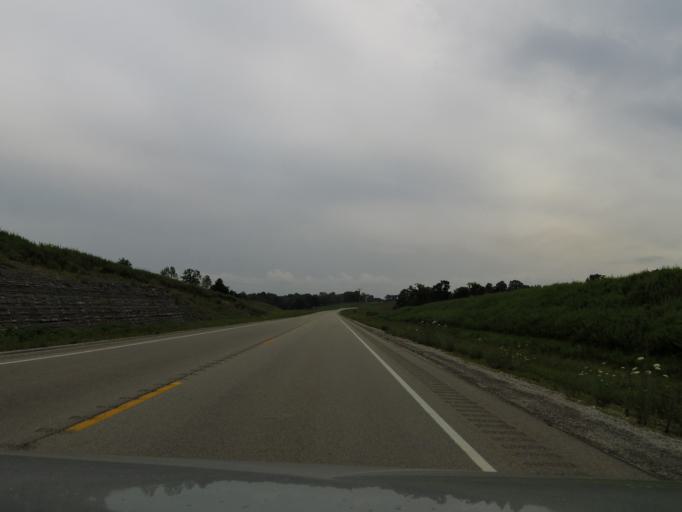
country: US
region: Ohio
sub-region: Brown County
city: Aberdeen
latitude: 38.6010
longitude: -83.8239
